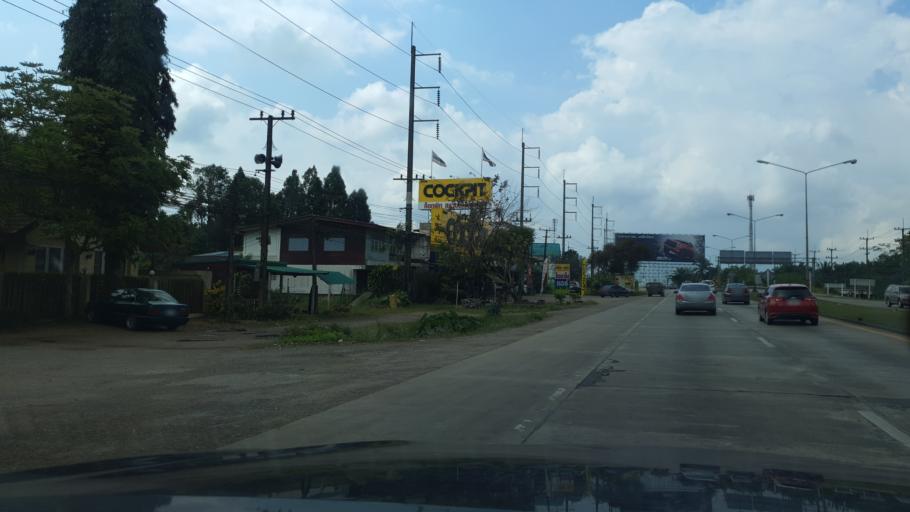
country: TH
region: Chumphon
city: Tha Sae
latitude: 10.6614
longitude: 99.1954
